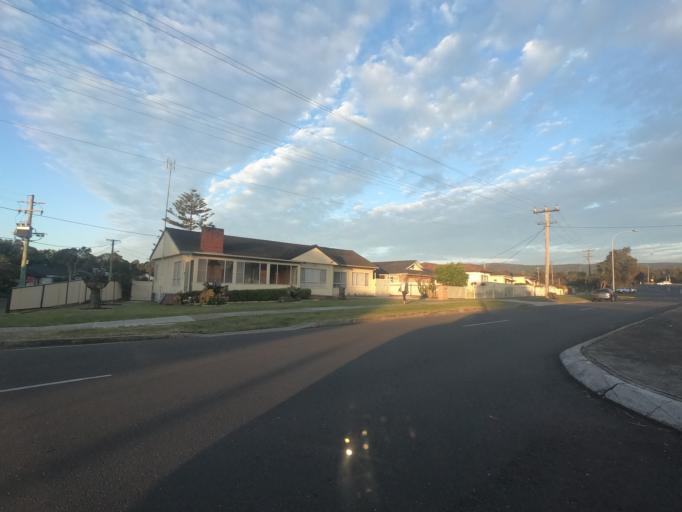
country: AU
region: New South Wales
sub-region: Wollongong
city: Koonawarra
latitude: -34.5002
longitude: 150.7994
